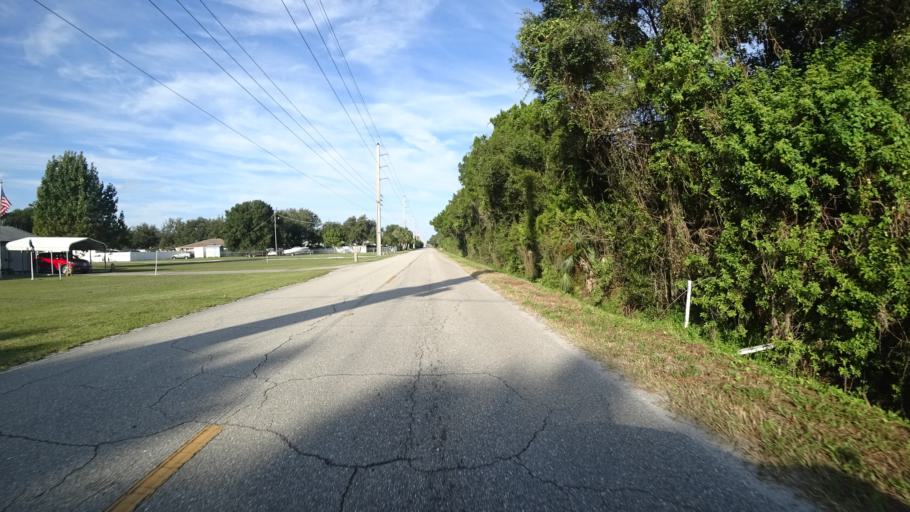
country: US
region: Florida
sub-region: Manatee County
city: Samoset
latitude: 27.4618
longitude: -82.4987
